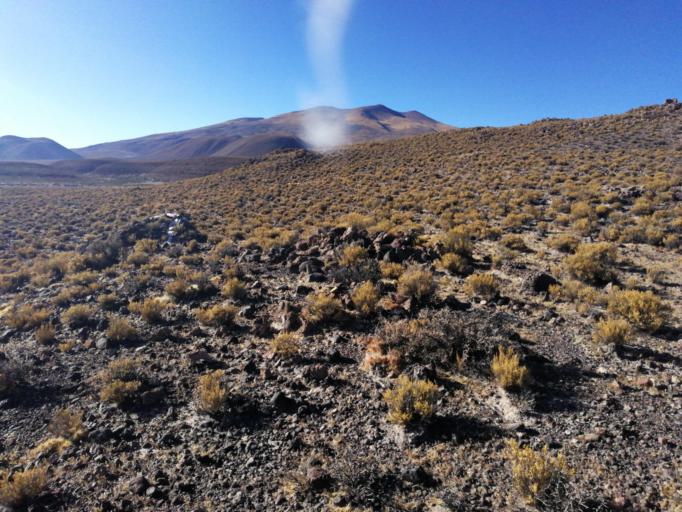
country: BO
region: Oruro
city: Cruz de Machacamarca
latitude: -19.2587
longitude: -68.3218
